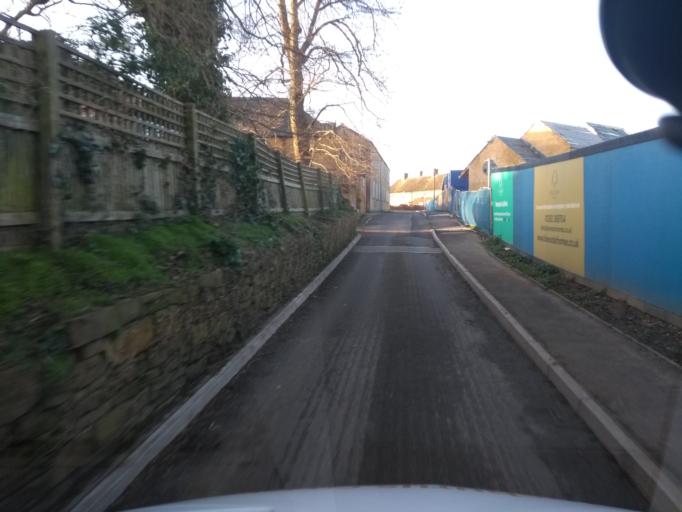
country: GB
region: England
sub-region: Somerset
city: Stoke-sub-Hamdon
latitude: 50.9552
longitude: -2.7529
